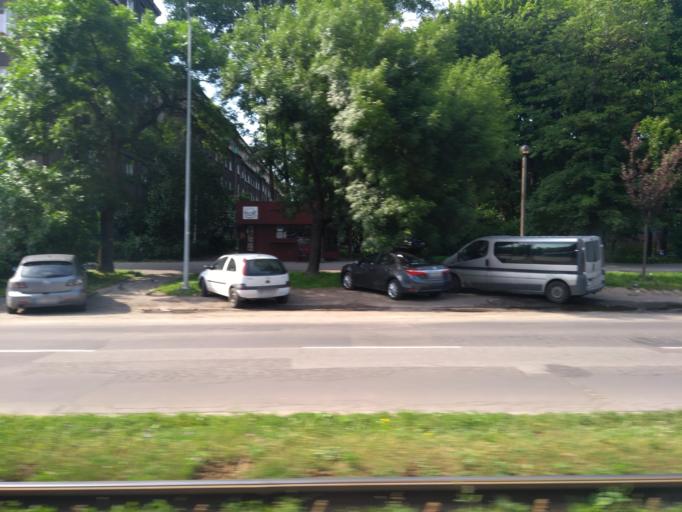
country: PL
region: Lesser Poland Voivodeship
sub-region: Powiat wielicki
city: Kokotow
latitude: 50.0757
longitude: 20.0505
